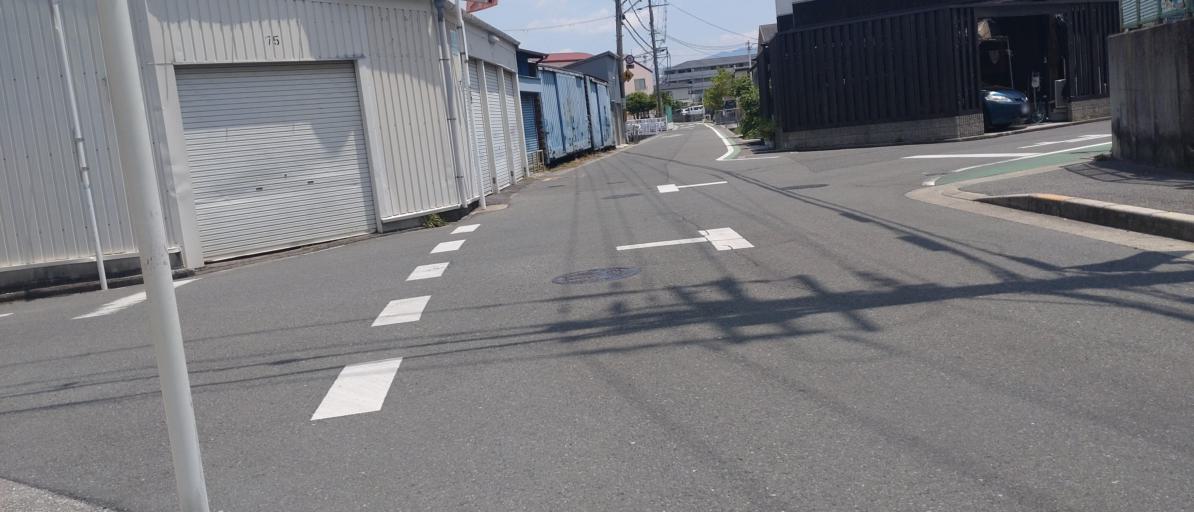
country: JP
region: Osaka
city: Matsubara
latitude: 34.5223
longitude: 135.5509
